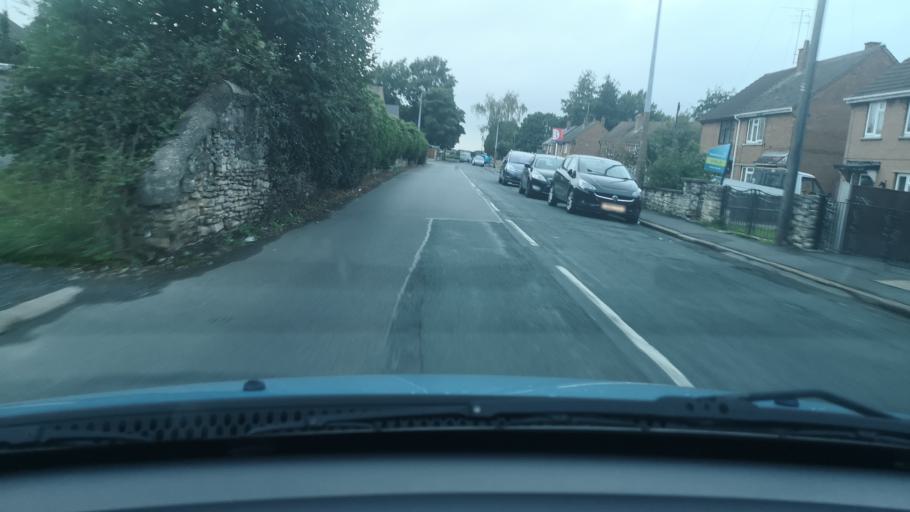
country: GB
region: England
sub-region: Doncaster
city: Campsall
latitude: 53.6219
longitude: -1.1792
